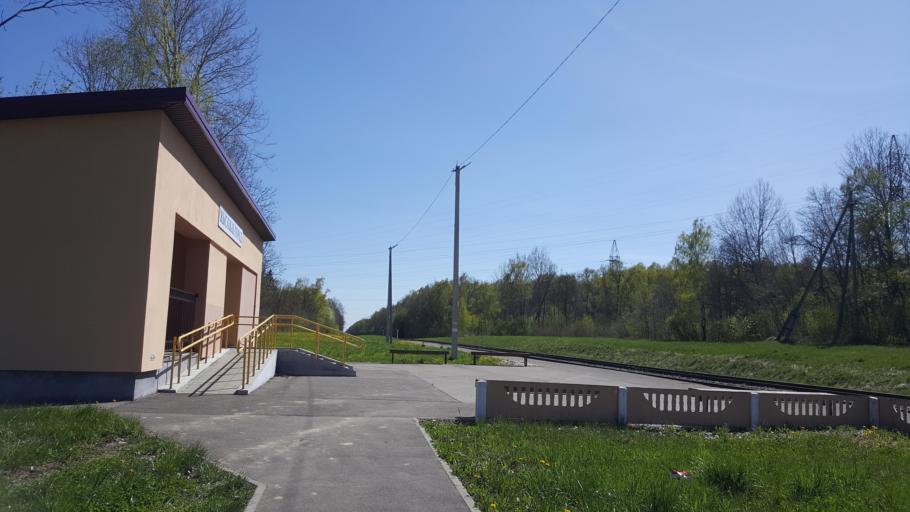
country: BY
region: Brest
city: Vysokaye
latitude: 52.3573
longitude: 23.4158
